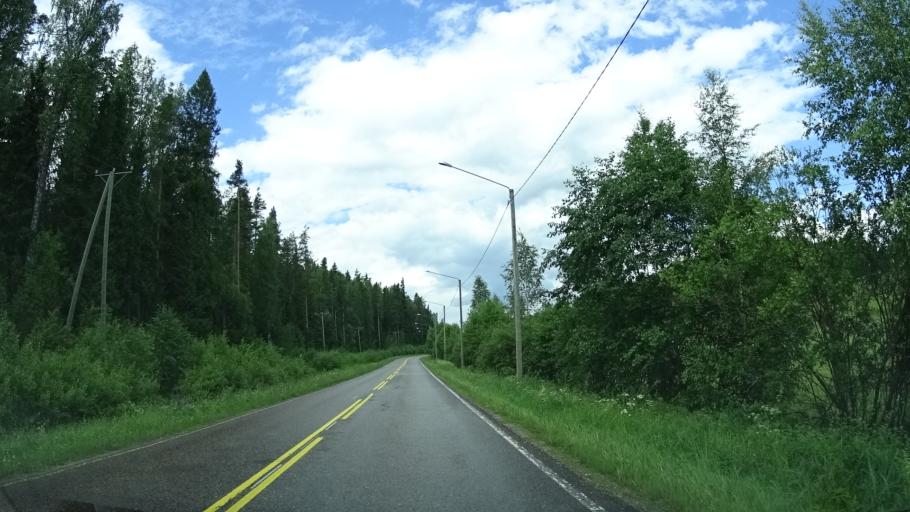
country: FI
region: Uusimaa
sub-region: Helsinki
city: Espoo
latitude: 60.3565
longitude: 24.6446
